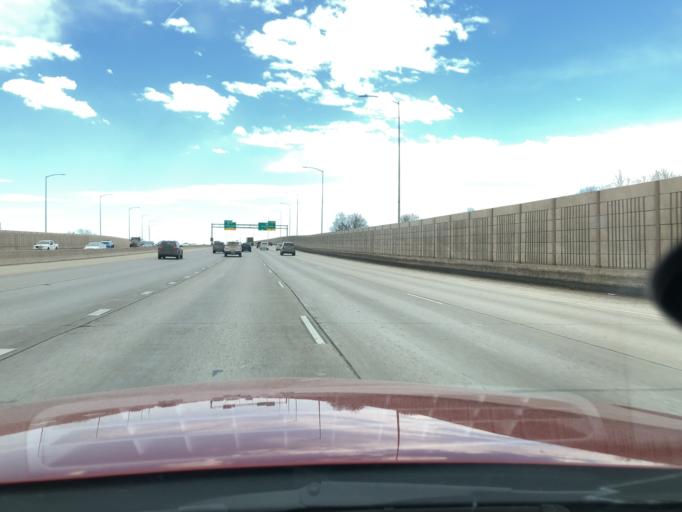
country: US
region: Colorado
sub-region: Jefferson County
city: Arvada
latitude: 39.7836
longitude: -105.0951
